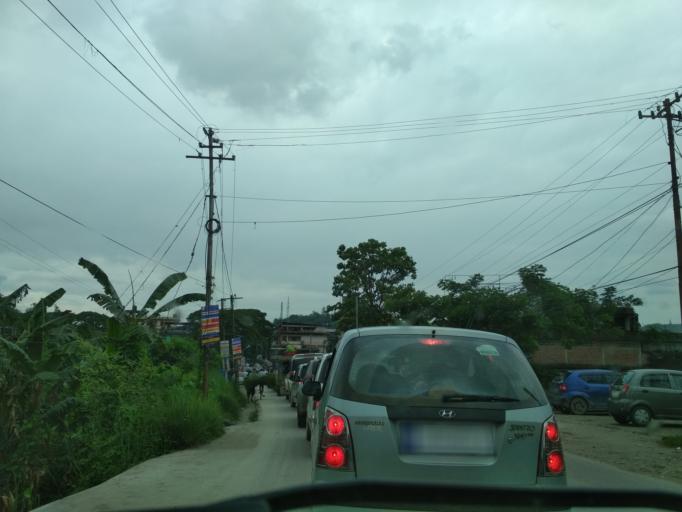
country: IN
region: Arunachal Pradesh
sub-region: Papum Pare
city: Naharlagun
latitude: 27.1003
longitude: 93.6866
